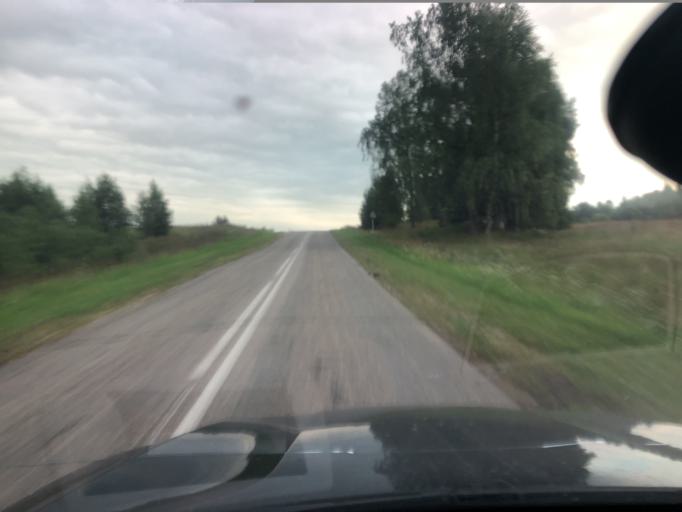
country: RU
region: Jaroslavl
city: Petrovsk
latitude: 57.0055
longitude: 39.0180
